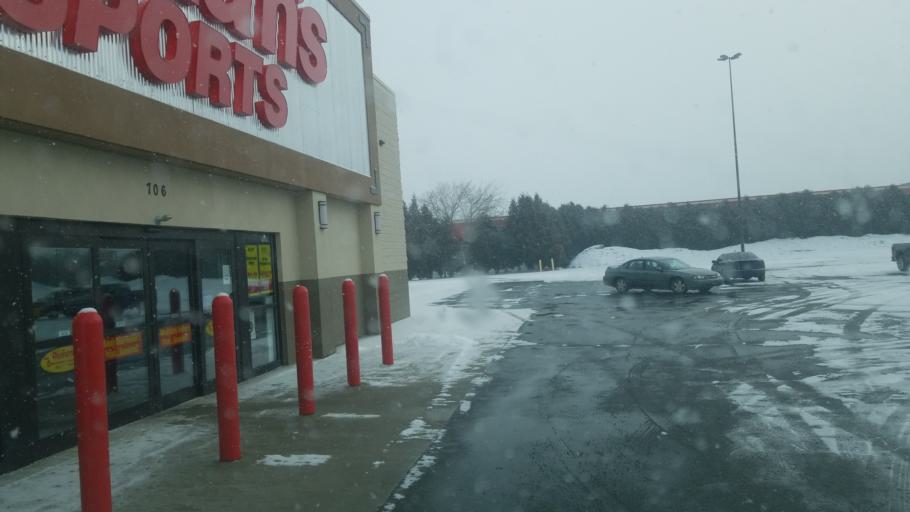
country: US
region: Michigan
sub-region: Mecosta County
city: Big Rapids
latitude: 43.6888
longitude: -85.4906
